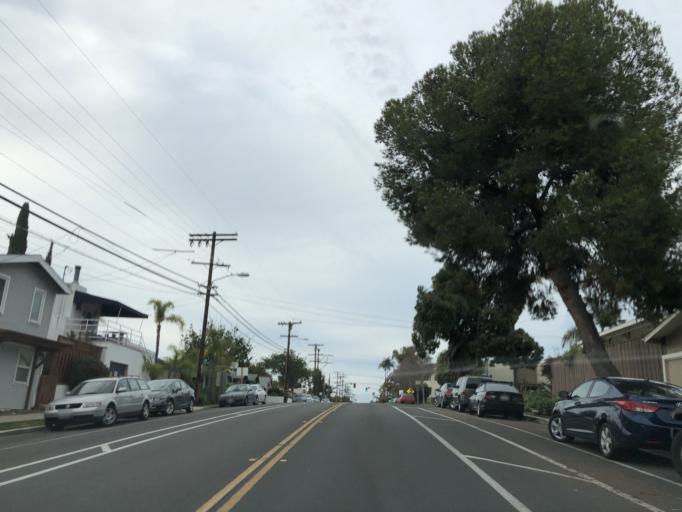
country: US
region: California
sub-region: San Diego County
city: San Diego
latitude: 32.7446
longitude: -117.1513
